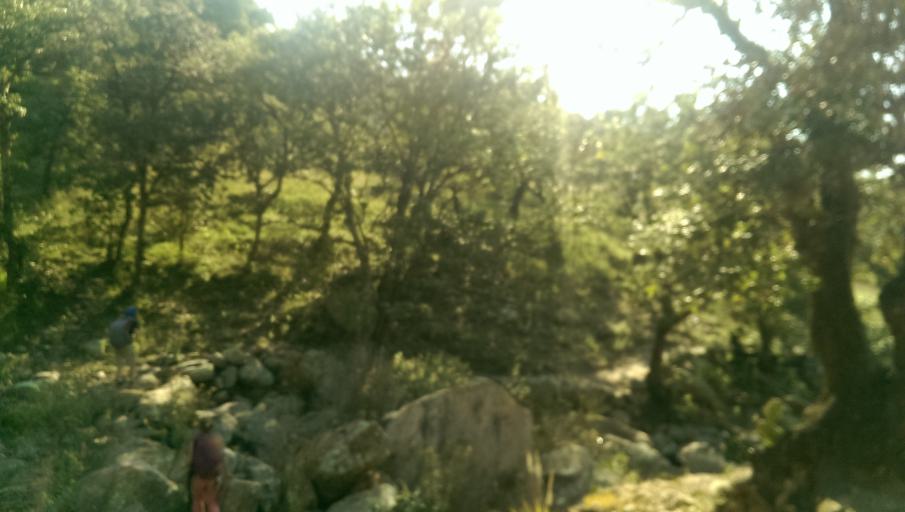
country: MX
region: Queretaro
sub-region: Huimilpan
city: San Jose Tepuzas
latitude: 20.3438
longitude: -100.3677
